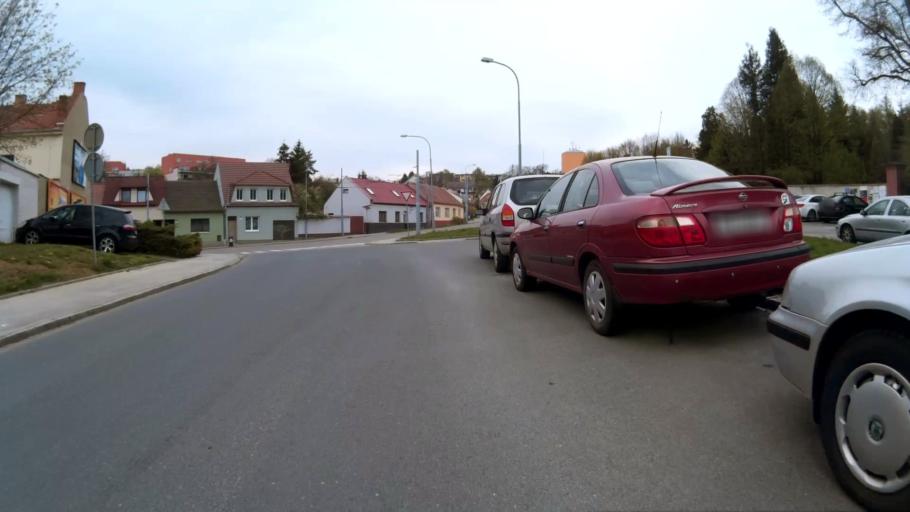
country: CZ
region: South Moravian
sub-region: Mesto Brno
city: Mokra Hora
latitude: 49.2222
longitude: 16.5567
